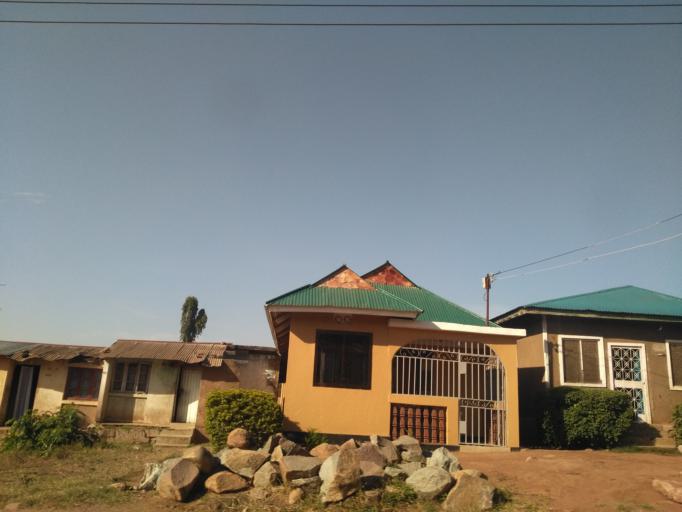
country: TZ
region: Mwanza
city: Mwanza
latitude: -2.5034
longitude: 32.8932
